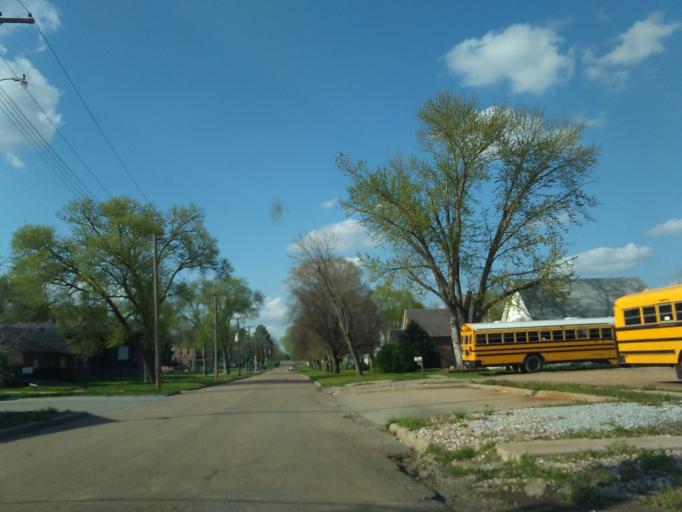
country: US
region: Nebraska
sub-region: Webster County
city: Red Cloud
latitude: 40.0899
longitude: -98.5206
